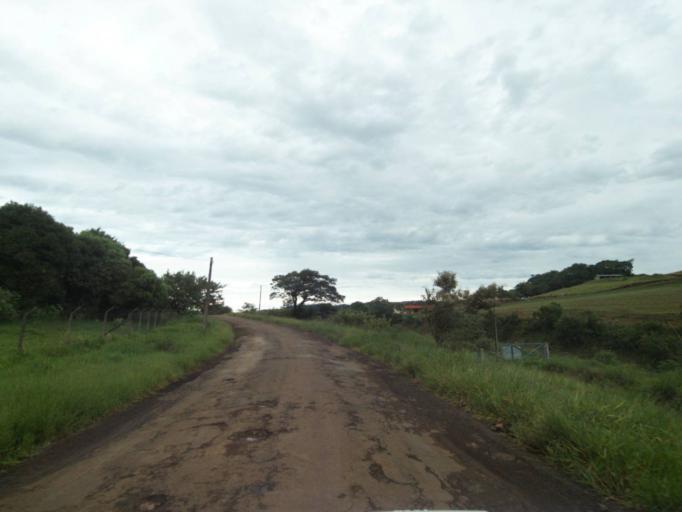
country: BR
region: Parana
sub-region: Guaraniacu
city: Guaraniacu
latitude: -25.1181
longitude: -52.8505
